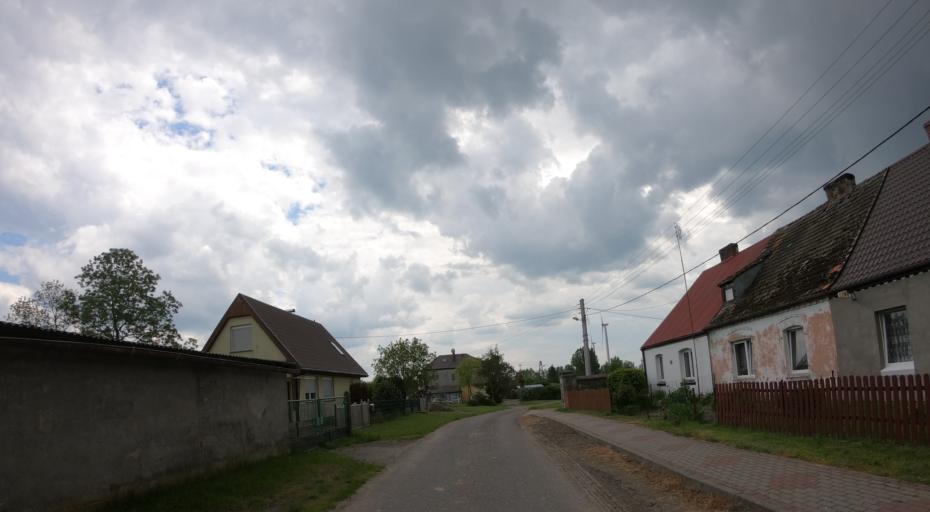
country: PL
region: West Pomeranian Voivodeship
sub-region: Powiat pyrzycki
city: Kozielice
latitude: 53.1494
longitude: 14.7913
